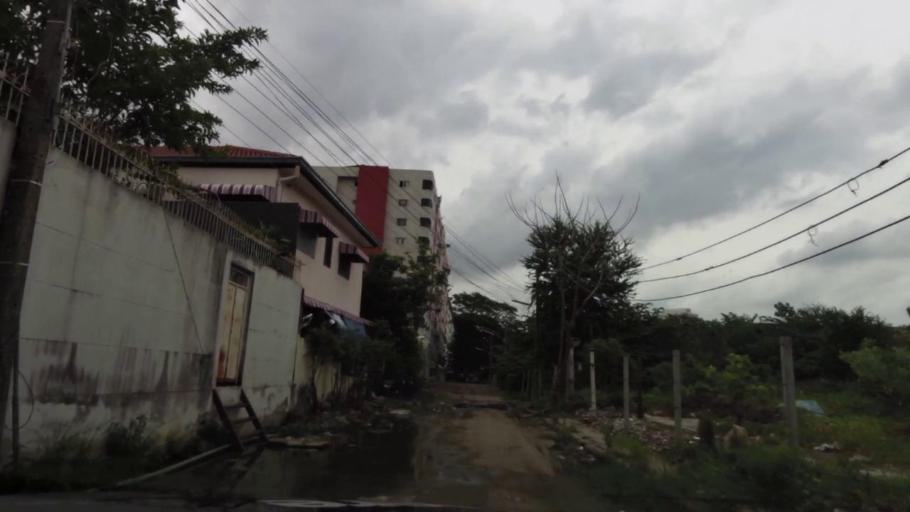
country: TH
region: Bangkok
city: Bang Kapi
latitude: 13.7701
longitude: 100.6452
